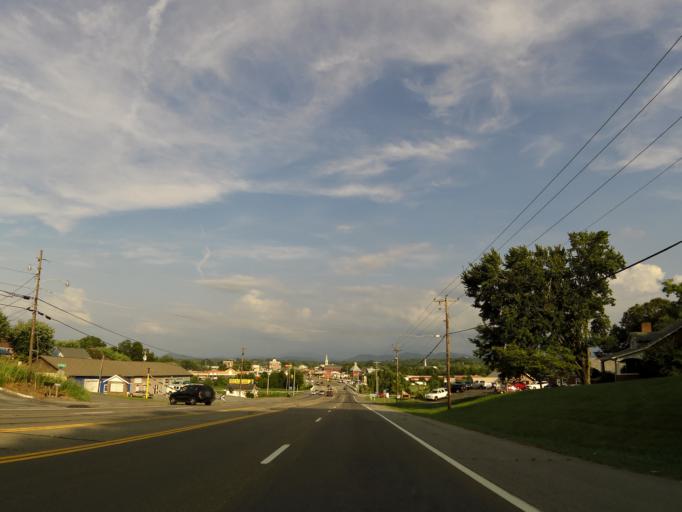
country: US
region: Tennessee
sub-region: Sevier County
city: Sevierville
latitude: 35.8726
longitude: -83.5770
